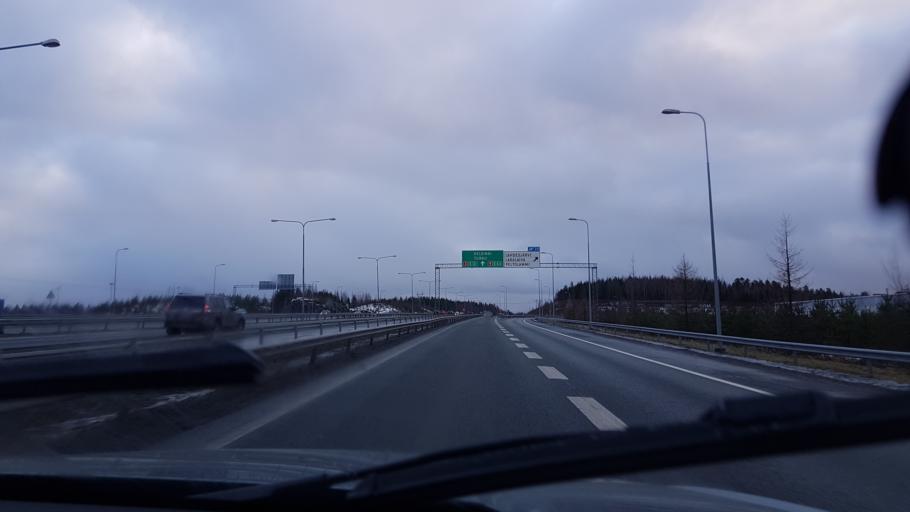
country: FI
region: Pirkanmaa
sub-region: Tampere
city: Tampere
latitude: 61.4538
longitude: 23.7670
